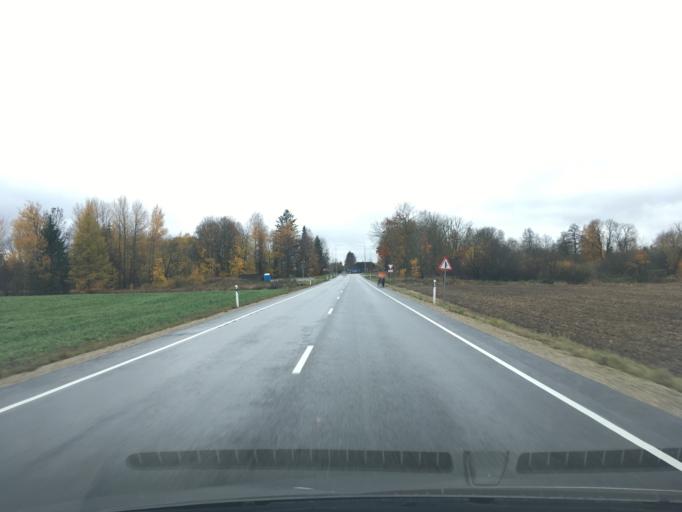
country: EE
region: Jogevamaa
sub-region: Tabivere vald
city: Tabivere
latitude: 58.4324
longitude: 26.4876
